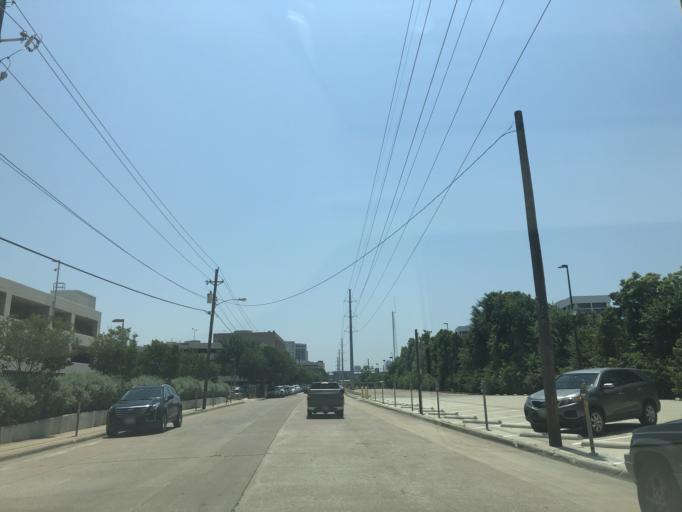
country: US
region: Texas
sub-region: Dallas County
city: Dallas
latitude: 32.8121
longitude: -96.8466
